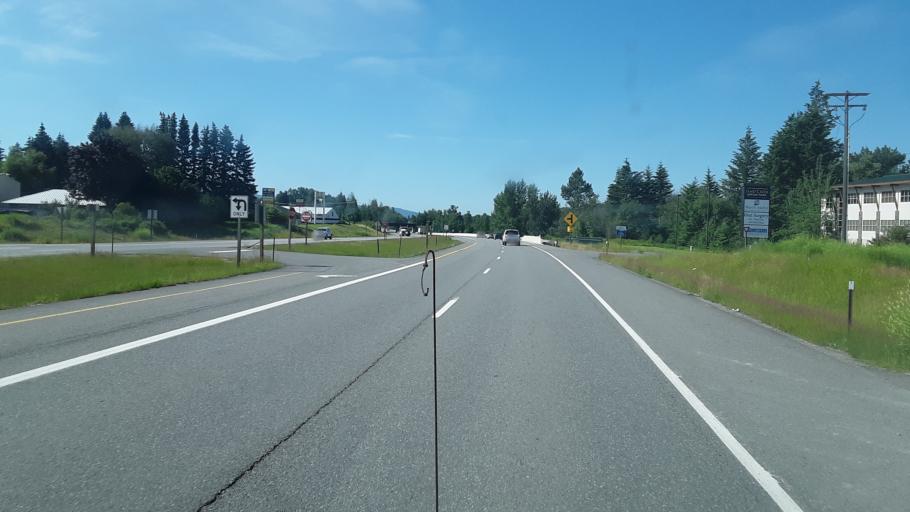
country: US
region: Idaho
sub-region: Bonner County
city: Ponderay
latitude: 48.2999
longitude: -116.5475
